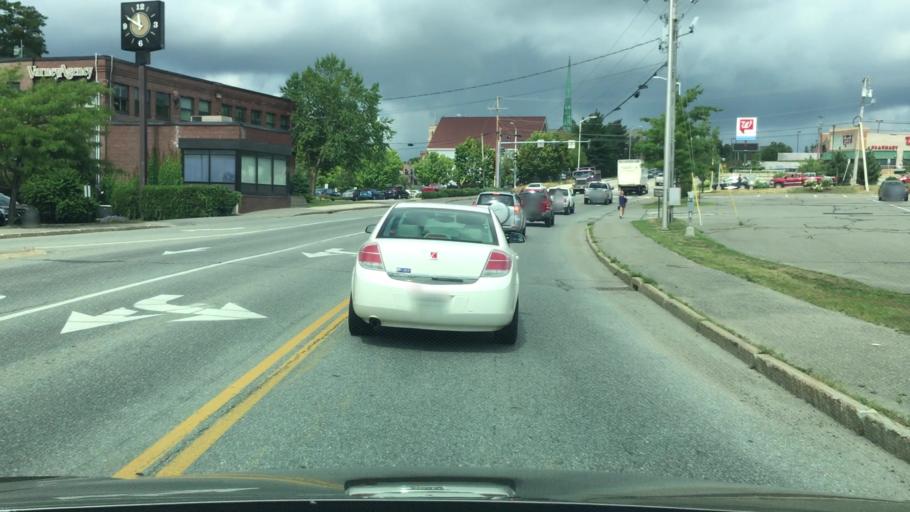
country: US
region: Maine
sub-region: Penobscot County
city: Brewer
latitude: 44.8002
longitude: -68.7660
